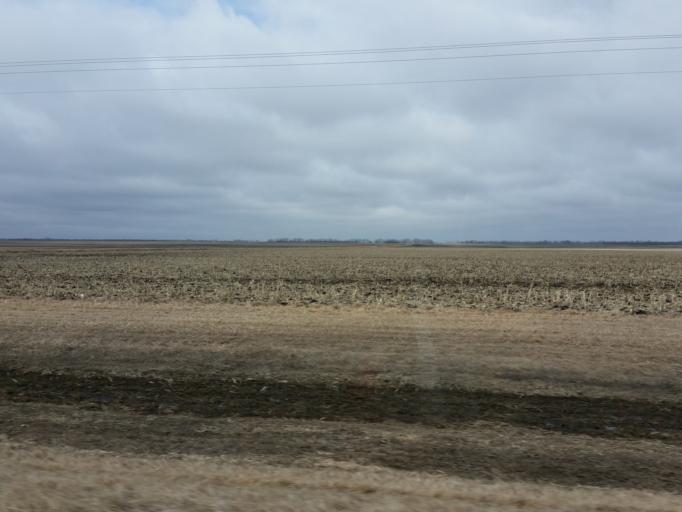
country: US
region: North Dakota
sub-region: Traill County
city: Mayville
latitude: 47.3830
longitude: -97.3265
